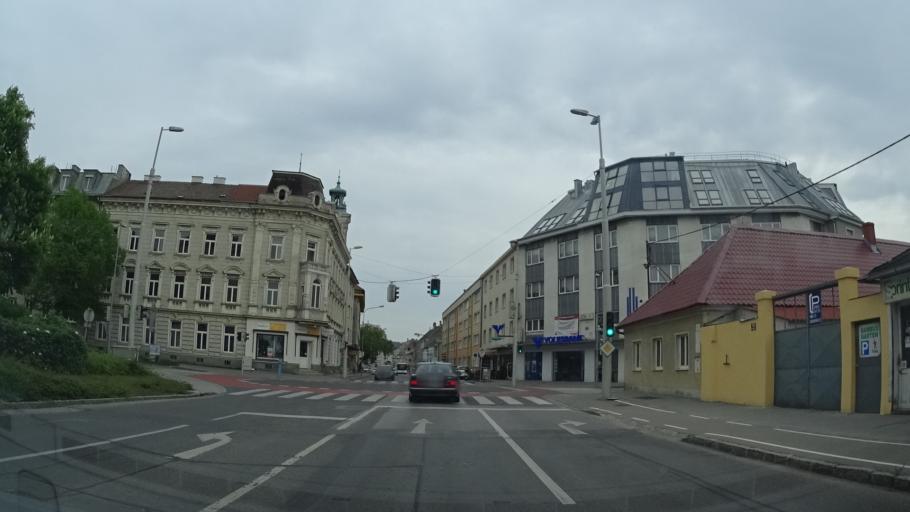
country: AT
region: Lower Austria
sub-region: Politischer Bezirk Korneuburg
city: Korneuburg
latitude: 48.3460
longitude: 16.3303
